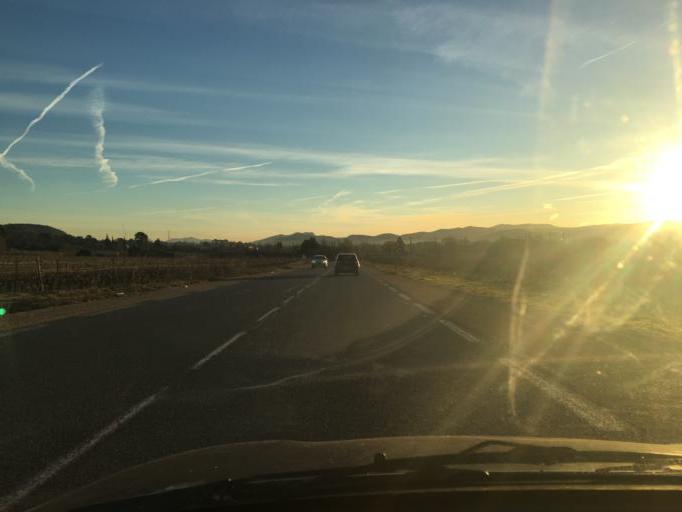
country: FR
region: Provence-Alpes-Cote d'Azur
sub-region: Departement du Var
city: Taradeau
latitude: 43.4496
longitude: 6.4451
